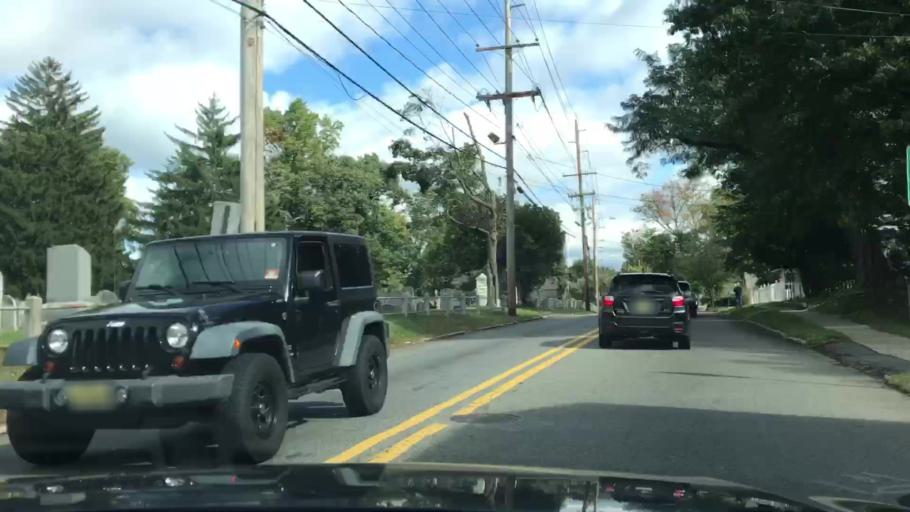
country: US
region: New Jersey
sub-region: Bergen County
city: Dumont
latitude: 40.9402
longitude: -74.0032
